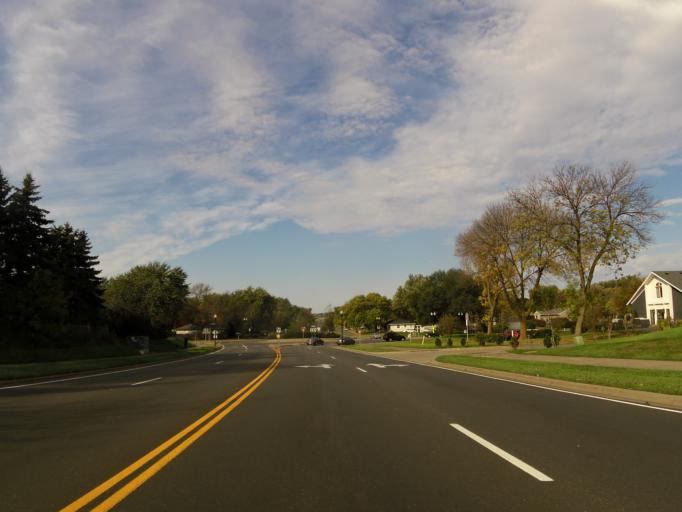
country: US
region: Minnesota
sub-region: Dakota County
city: Eagan
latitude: 44.8047
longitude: -93.2062
